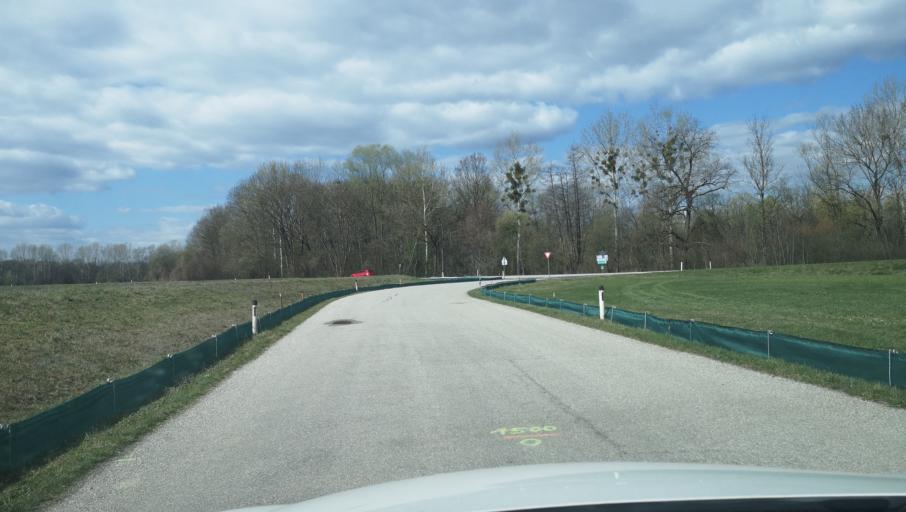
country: AT
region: Lower Austria
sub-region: Politischer Bezirk Amstetten
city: Euratsfeld
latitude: 48.1013
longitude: 14.9389
